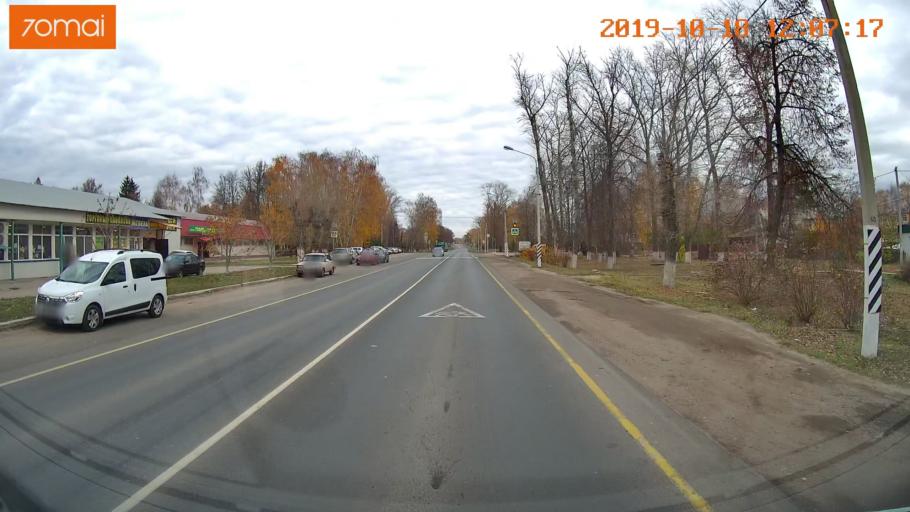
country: RU
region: Rjazan
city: Zakharovo
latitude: 54.3682
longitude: 39.2768
